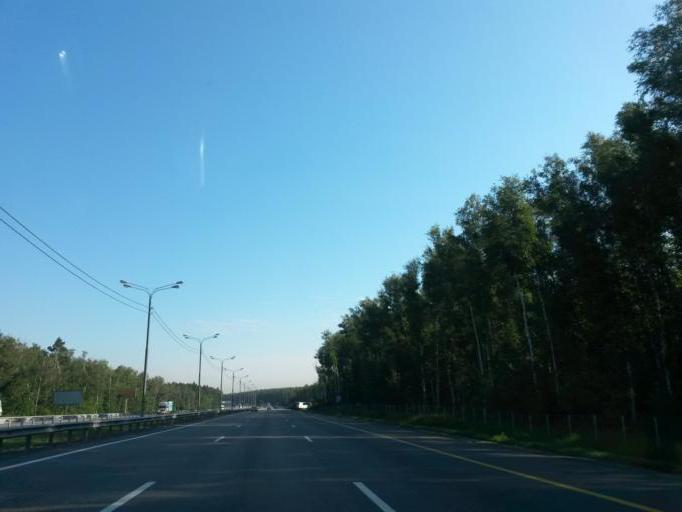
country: RU
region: Moskovskaya
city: Vostryakovo
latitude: 55.4314
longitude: 37.7984
